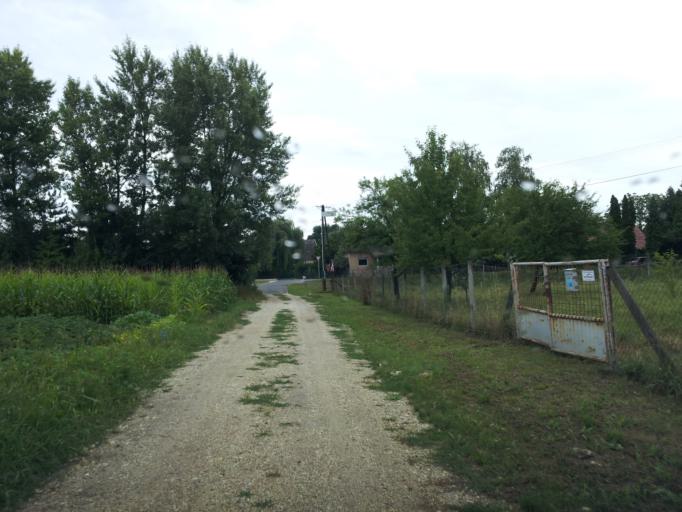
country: HU
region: Vas
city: Kormend
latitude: 46.9559
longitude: 16.6438
